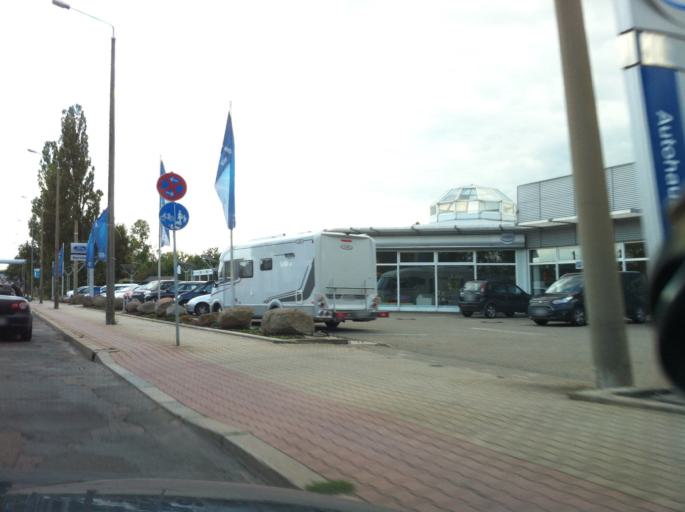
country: DE
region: Saxony
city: Leipzig
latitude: 51.3105
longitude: 12.3259
